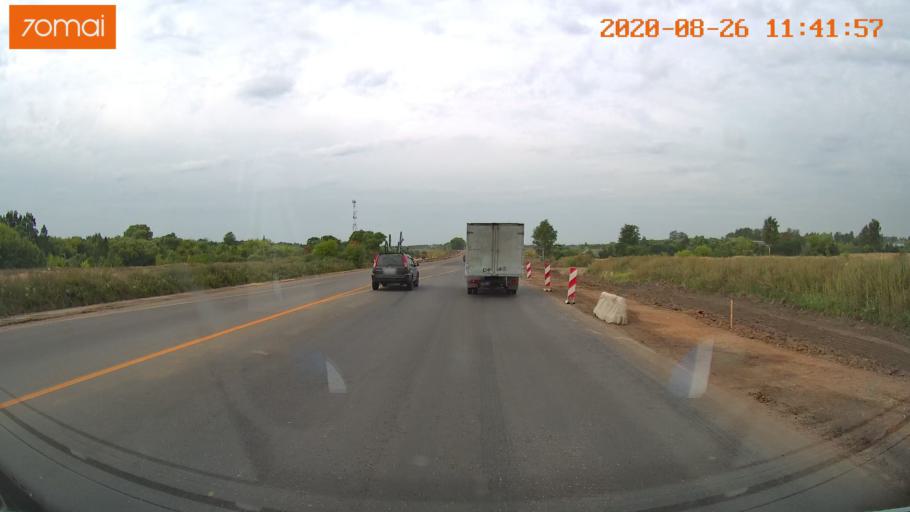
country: RU
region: Rjazan
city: Shilovo
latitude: 54.2961
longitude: 40.7014
